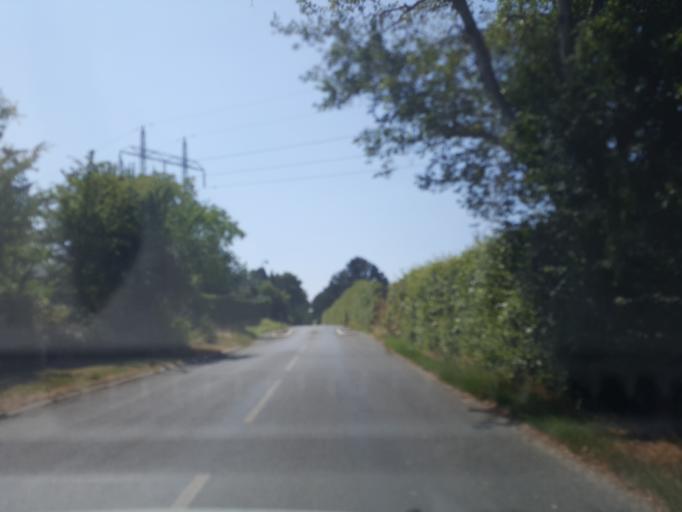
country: DK
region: Capital Region
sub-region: Fredensborg Kommune
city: Kokkedal
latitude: 55.9278
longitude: 12.4647
